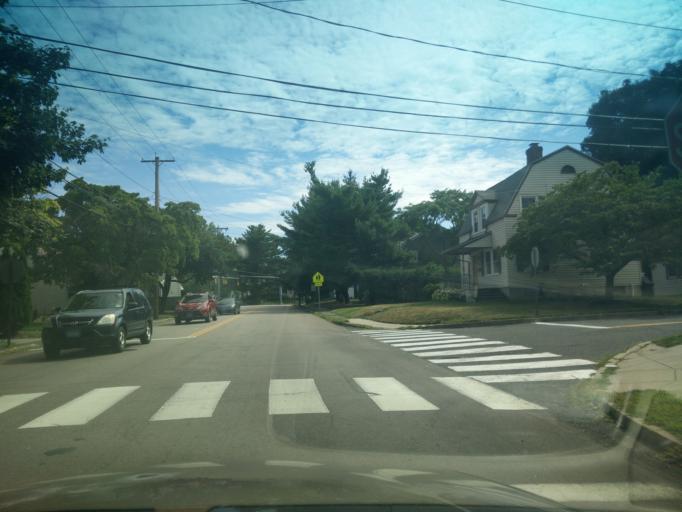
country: US
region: Connecticut
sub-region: Fairfield County
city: Bridgeport
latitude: 41.1795
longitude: -73.2360
